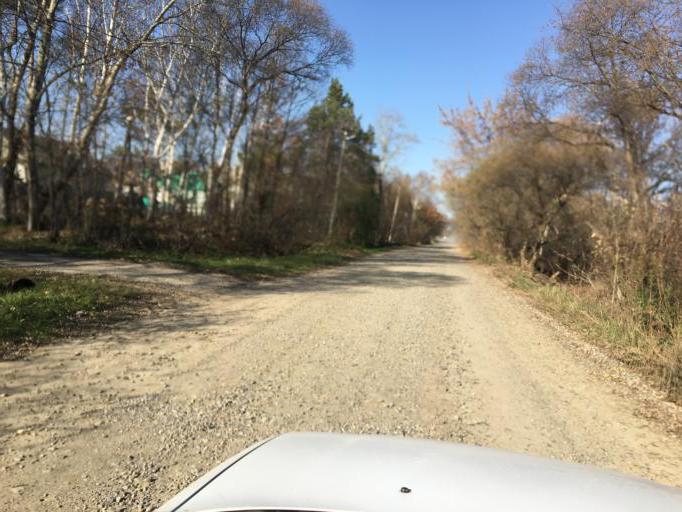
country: RU
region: Primorskiy
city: Dal'nerechensk
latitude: 45.9160
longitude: 133.7151
